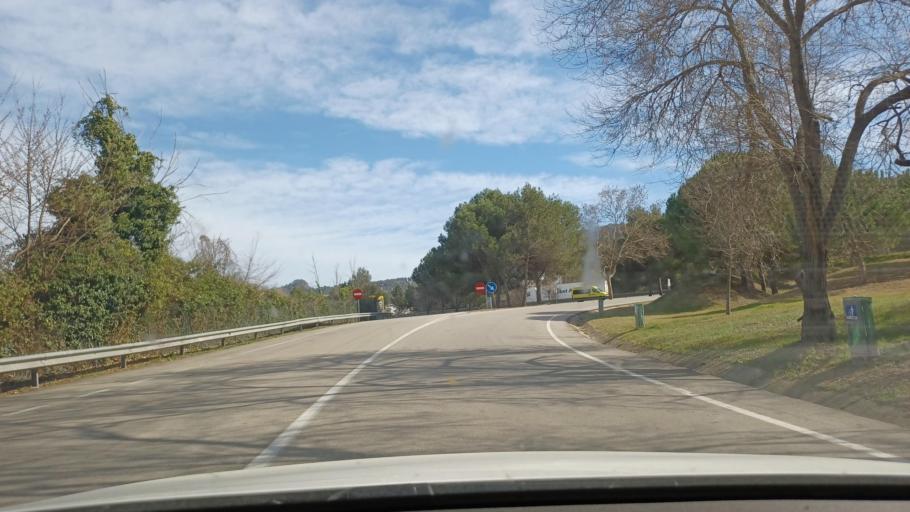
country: ES
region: Catalonia
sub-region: Provincia de Barcelona
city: Castellvi de Rosanes
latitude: 41.4551
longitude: 1.8840
